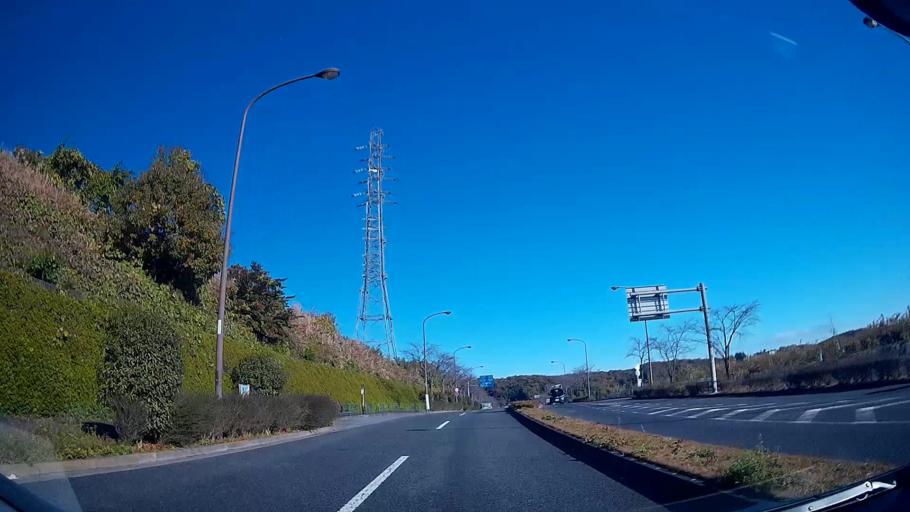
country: JP
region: Tokyo
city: Hachioji
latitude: 35.6829
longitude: 139.3390
